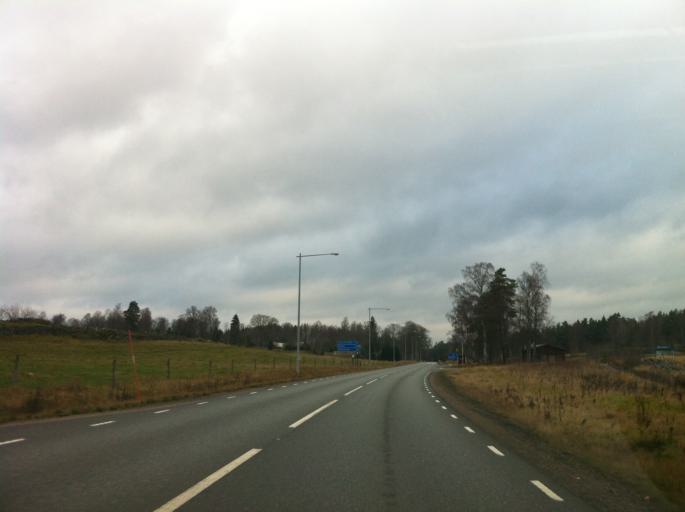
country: SE
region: Kronoberg
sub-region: Uppvidinge Kommun
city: Aseda
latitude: 57.4023
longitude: 15.3191
